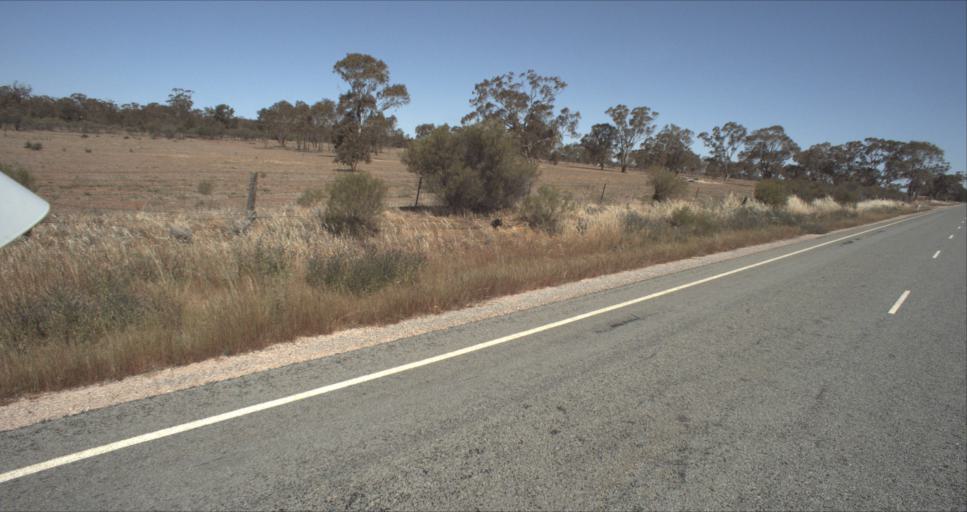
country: AU
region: New South Wales
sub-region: Leeton
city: Leeton
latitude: -34.4585
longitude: 146.4382
